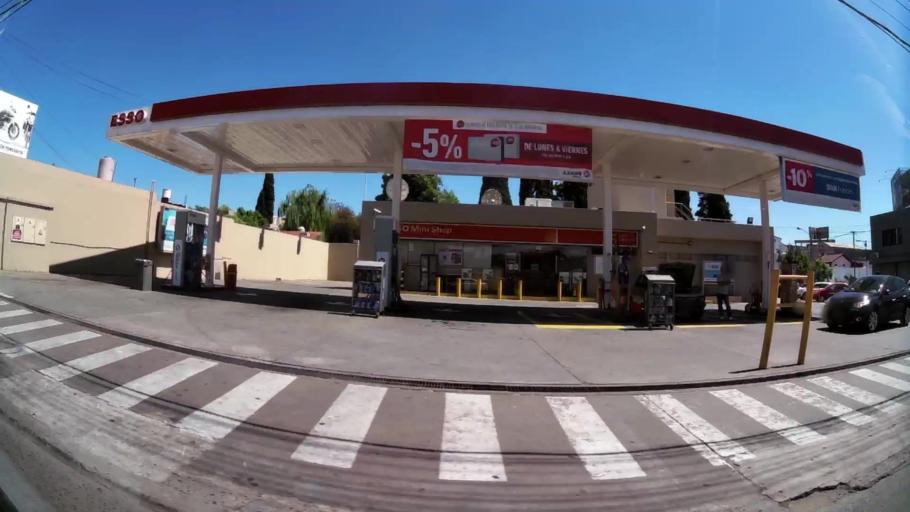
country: AR
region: Buenos Aires
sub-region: Partido de Tigre
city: Tigre
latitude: -34.4867
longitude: -58.6175
